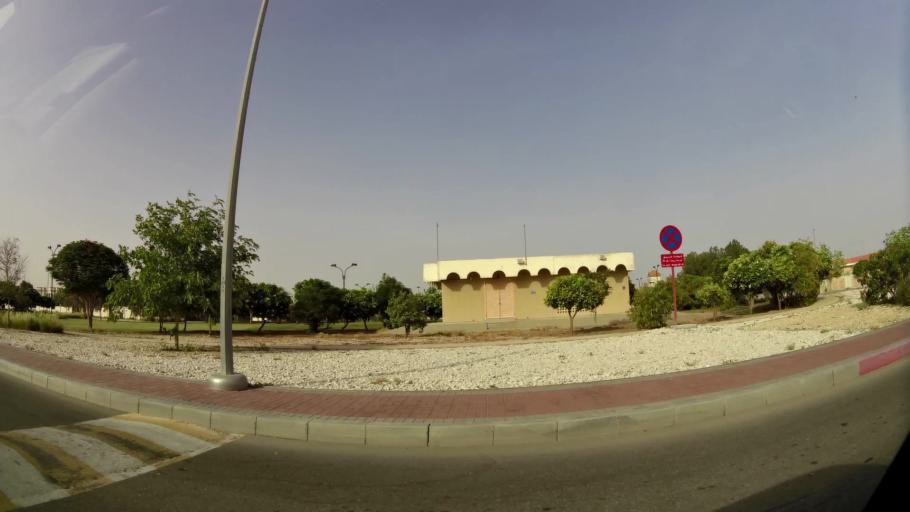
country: AE
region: Abu Dhabi
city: Al Ain
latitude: 24.2143
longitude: 55.6519
